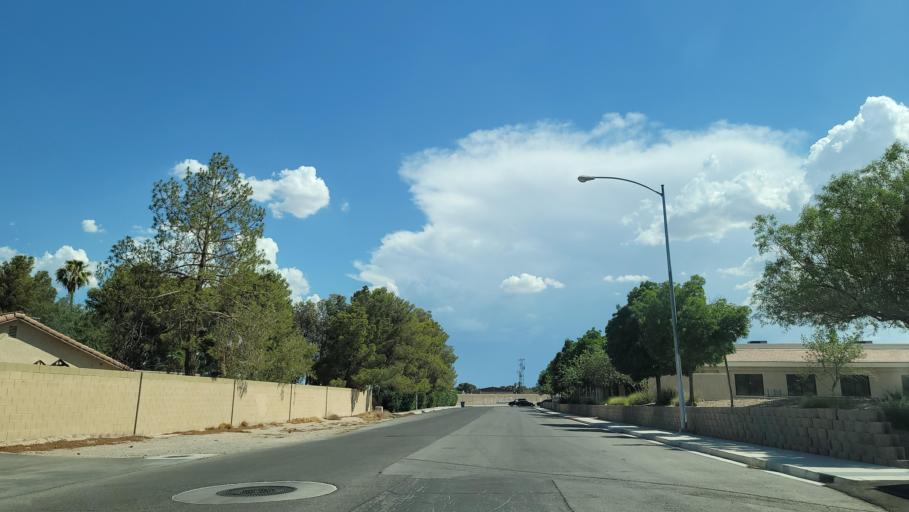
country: US
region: Nevada
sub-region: Clark County
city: Spring Valley
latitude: 36.1307
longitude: -115.2273
